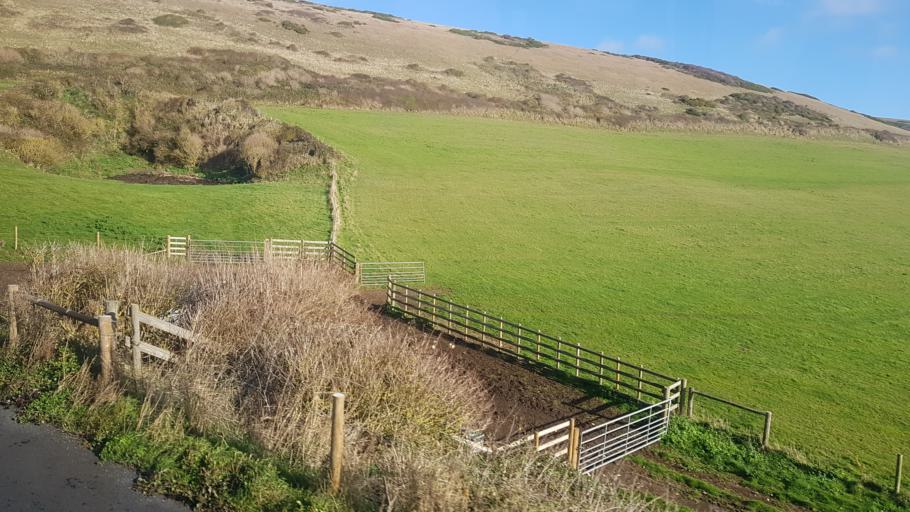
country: GB
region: England
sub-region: Isle of Wight
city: Freshwater
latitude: 50.6659
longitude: -1.4777
